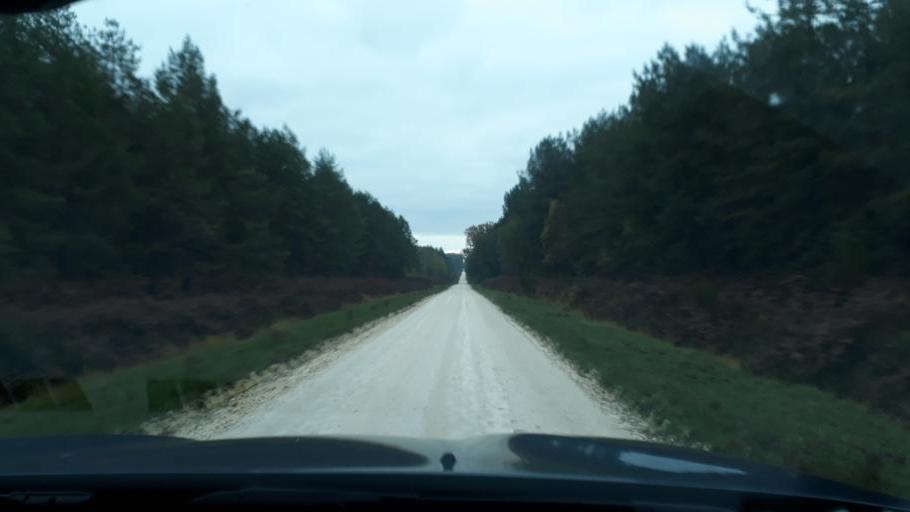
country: FR
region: Centre
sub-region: Departement du Loiret
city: Ouzouer-sur-Loire
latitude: 47.8376
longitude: 2.4570
